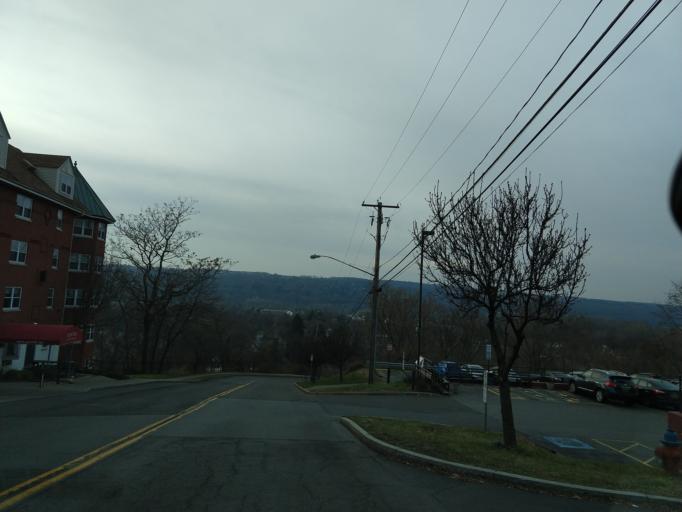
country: US
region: New York
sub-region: Tompkins County
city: Cayuga Heights
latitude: 42.4511
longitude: -76.4934
